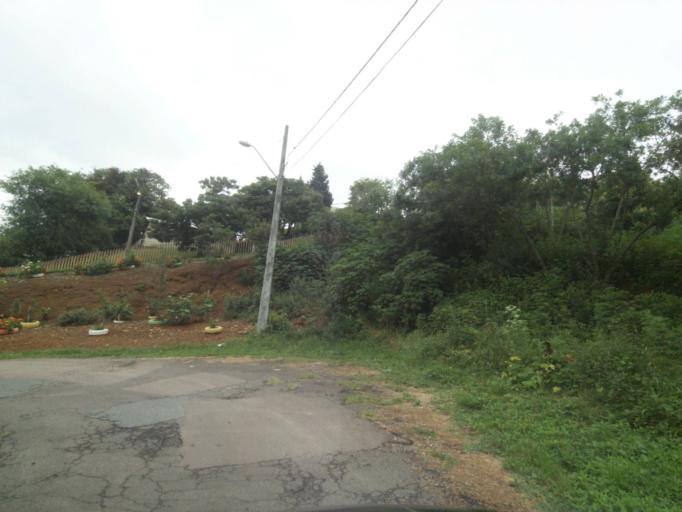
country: BR
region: Parana
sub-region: Curitiba
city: Curitiba
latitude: -25.4686
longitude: -49.3241
